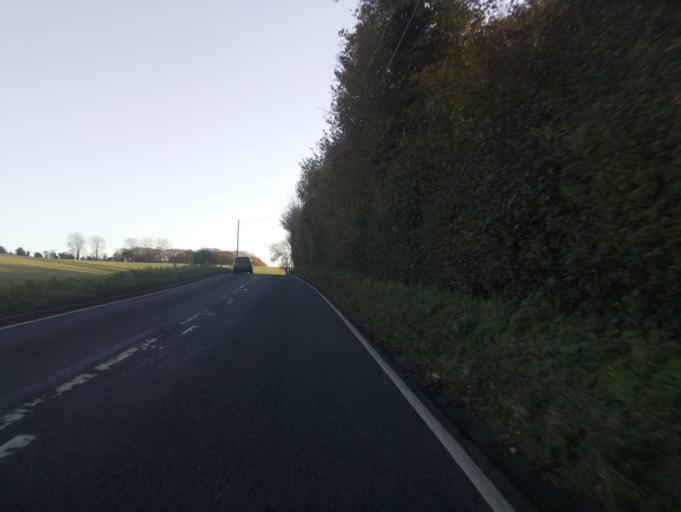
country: GB
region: England
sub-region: Wiltshire
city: Chicklade
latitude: 51.1270
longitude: -2.1632
